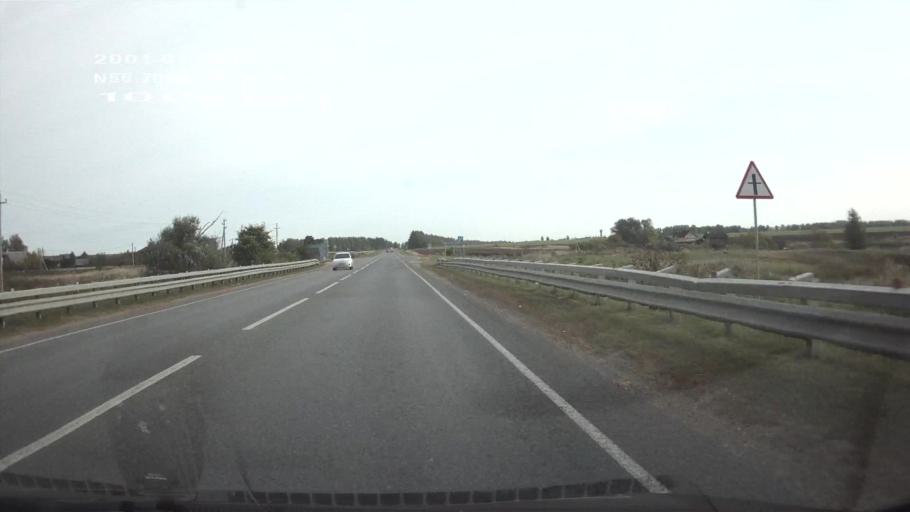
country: RU
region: Mariy-El
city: Yoshkar-Ola
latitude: 56.7099
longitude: 48.0843
